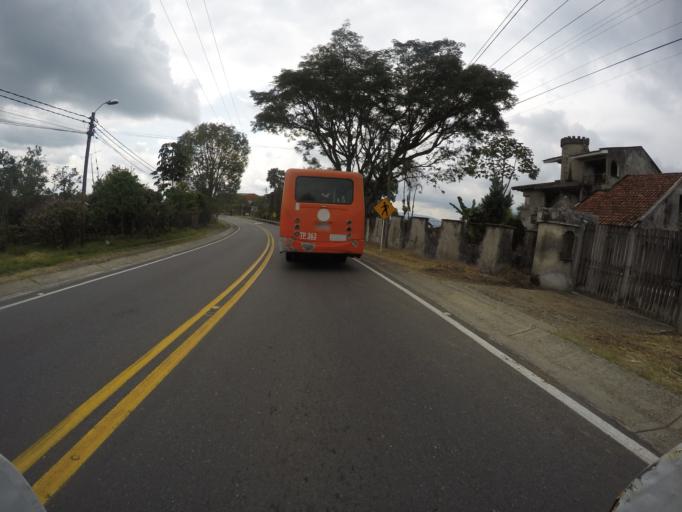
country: CO
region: Risaralda
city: Pereira
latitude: 4.7479
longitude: -75.6647
